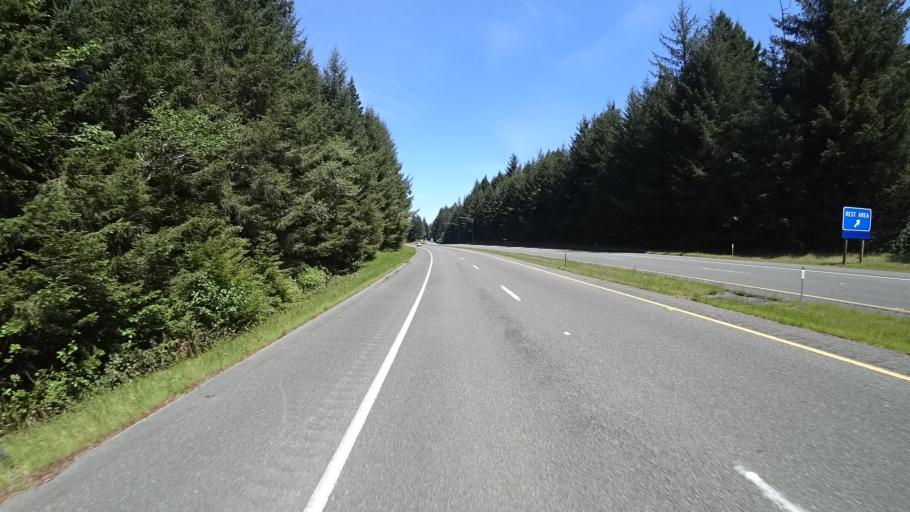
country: US
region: California
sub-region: Humboldt County
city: Westhaven-Moonstone
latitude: 41.1191
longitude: -124.1515
